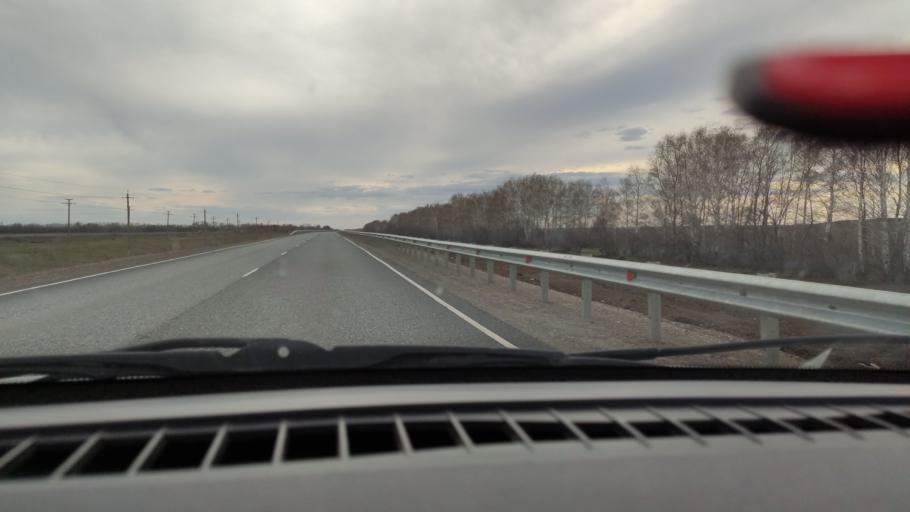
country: RU
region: Bashkortostan
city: Mayachnyy
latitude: 52.4107
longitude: 55.7442
